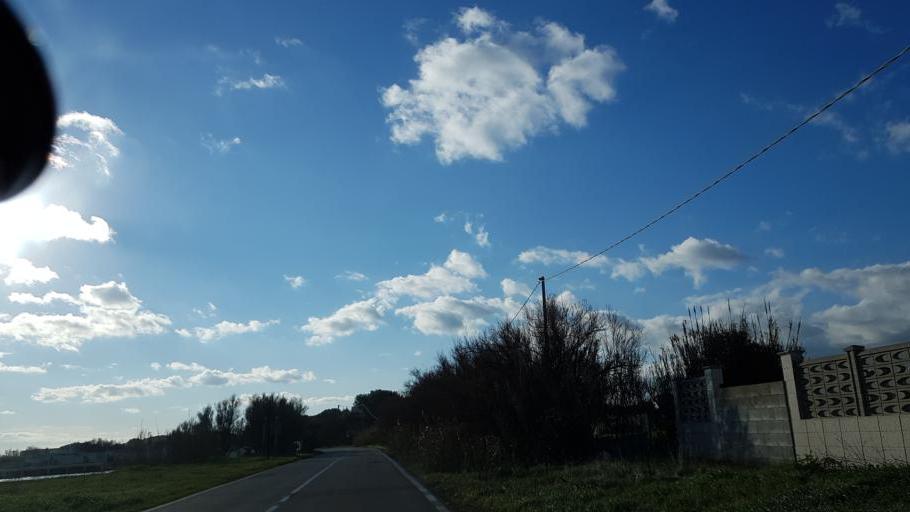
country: IT
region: Apulia
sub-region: Provincia di Brindisi
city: Materdomini
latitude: 40.6709
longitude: 17.9462
